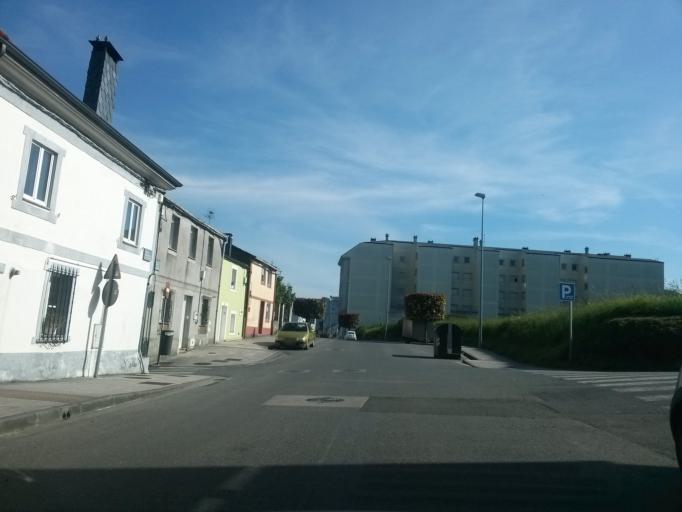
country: ES
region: Galicia
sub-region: Provincia de Lugo
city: Lugo
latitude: 43.0297
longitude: -7.5634
